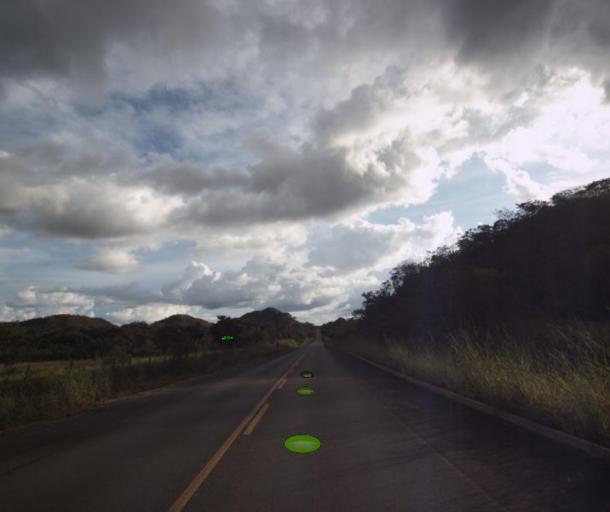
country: BR
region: Goias
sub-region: Niquelandia
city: Niquelandia
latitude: -14.5228
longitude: -48.5223
